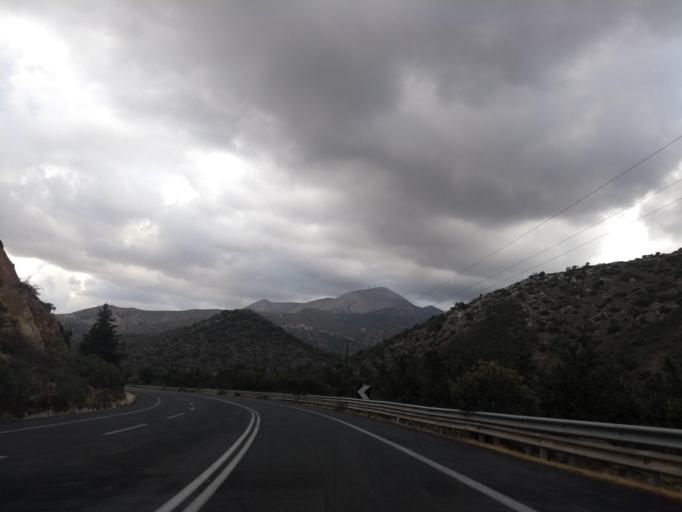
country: GR
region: Crete
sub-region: Nomos Rethymnis
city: Anogeia
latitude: 35.3880
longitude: 24.9369
